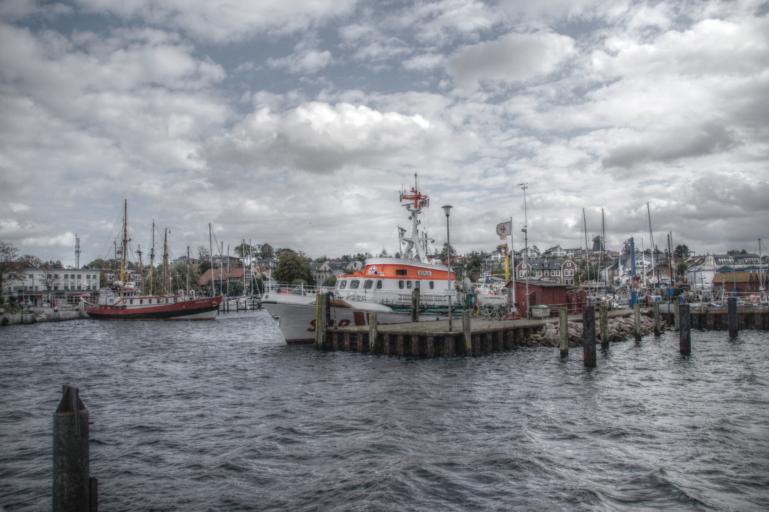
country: DE
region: Schleswig-Holstein
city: Laboe
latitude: 54.4038
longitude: 10.2175
